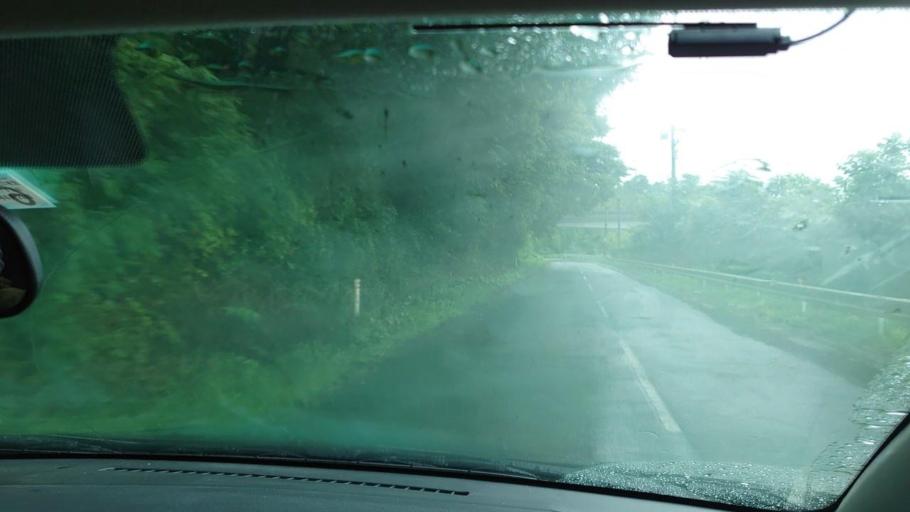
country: JP
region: Iwate
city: Ichinoseki
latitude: 38.7905
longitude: 141.2489
